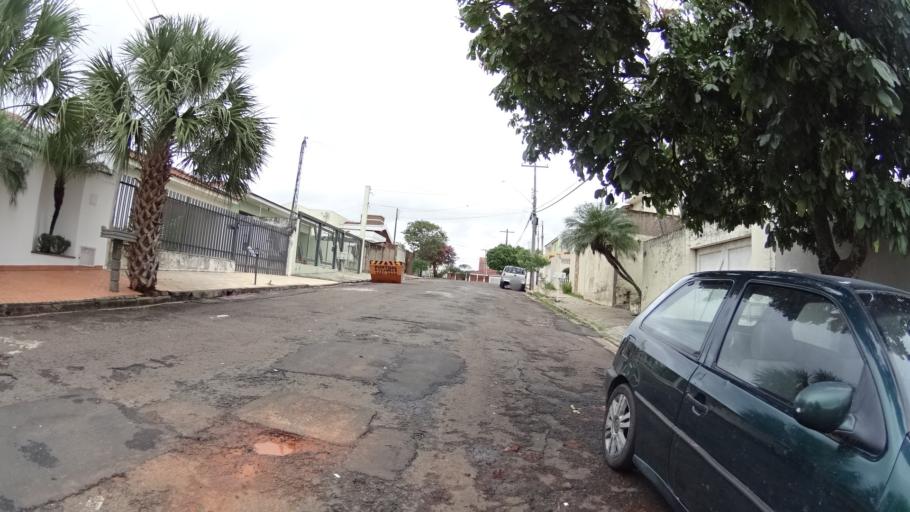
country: BR
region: Sao Paulo
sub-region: Marilia
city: Marilia
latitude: -22.2301
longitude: -49.9390
